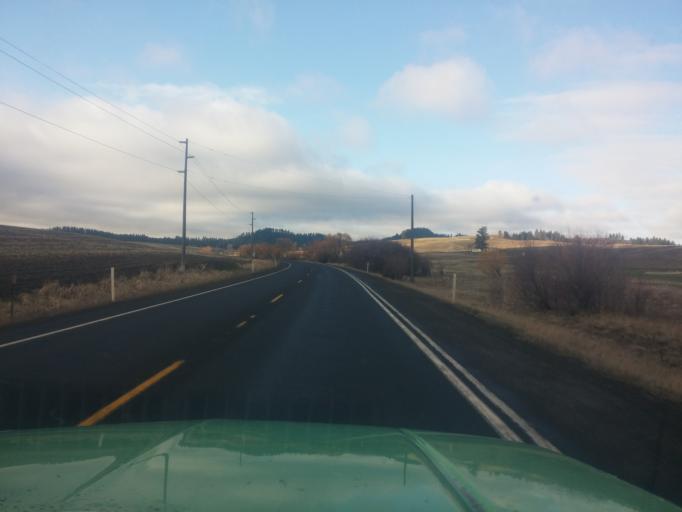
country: US
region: Idaho
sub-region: Latah County
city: Moscow
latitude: 46.8989
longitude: -116.9865
